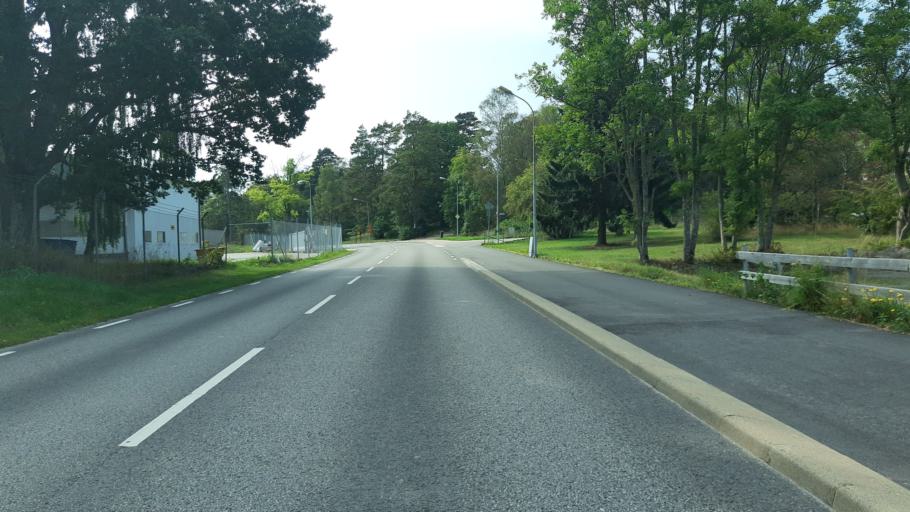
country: SE
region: Blekinge
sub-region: Ronneby Kommun
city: Ronneby
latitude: 56.1761
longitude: 15.2973
